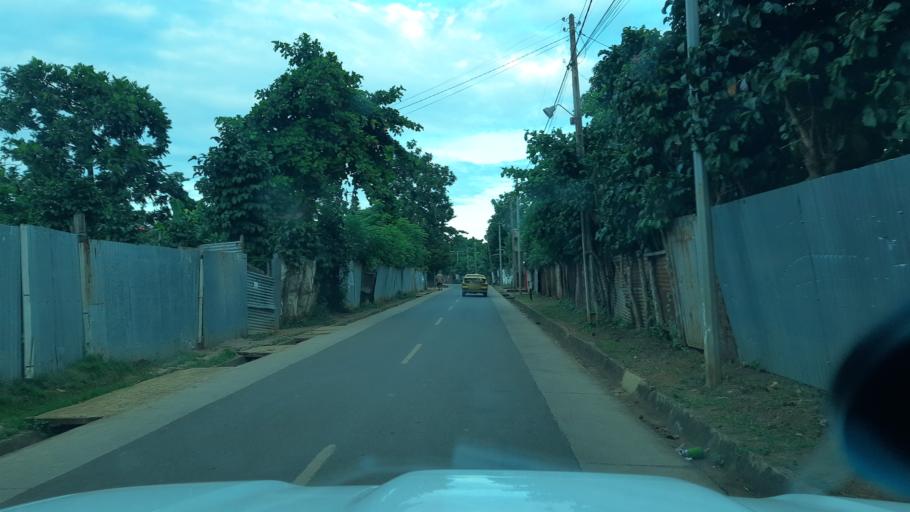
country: ST
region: Sao Tome Island
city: Sao Tome
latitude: 0.3017
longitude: 6.7487
